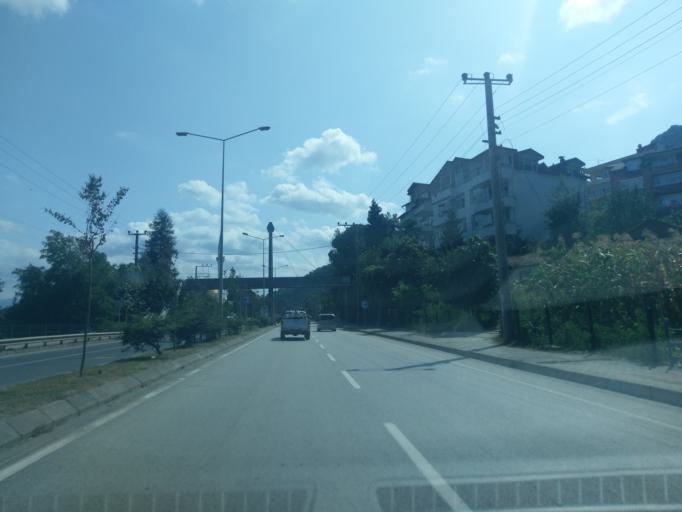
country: TR
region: Ordu
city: Ordu
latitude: 41.0050
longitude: 37.8699
